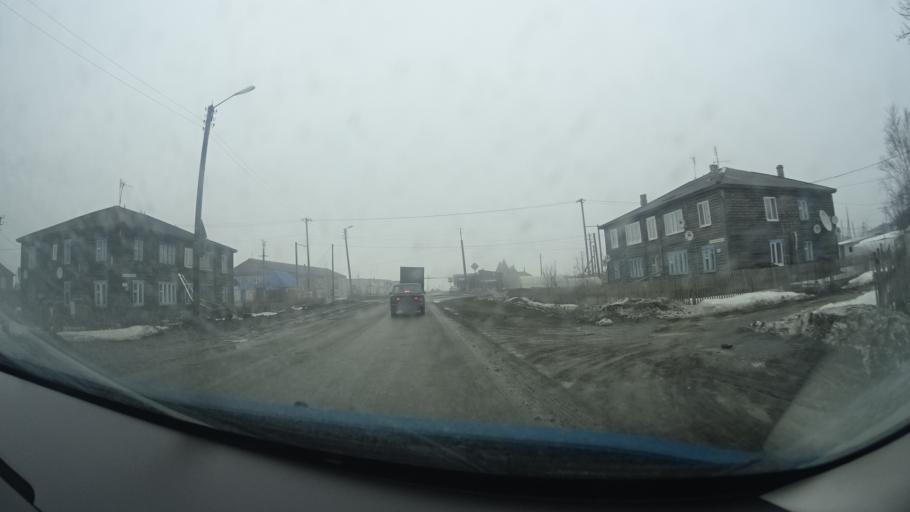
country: RU
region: Perm
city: Kuyeda
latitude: 56.4313
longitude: 55.5762
